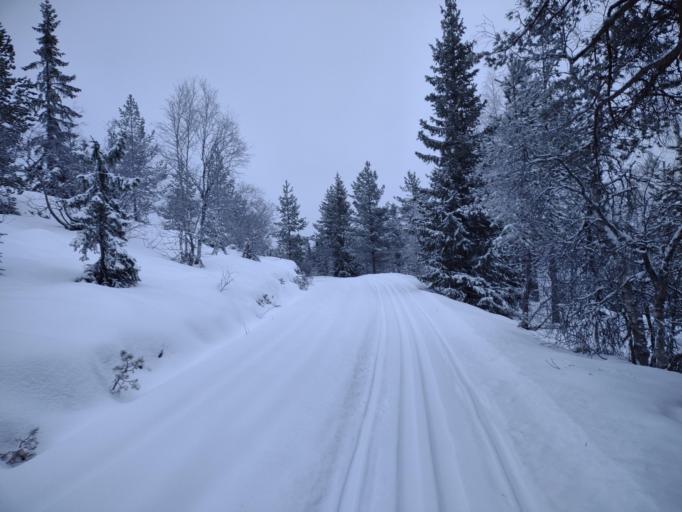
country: NO
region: Buskerud
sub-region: Flesberg
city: Lampeland
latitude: 59.7464
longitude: 9.4809
